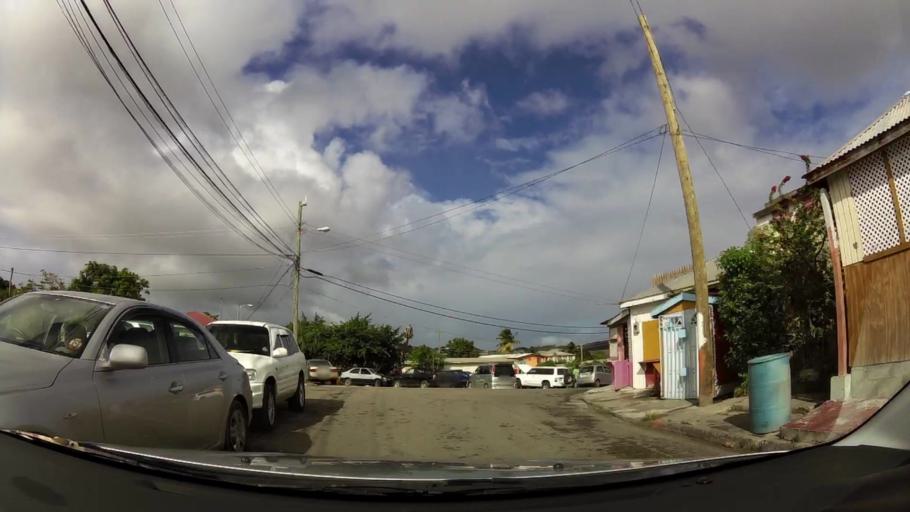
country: AG
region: Saint John
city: Saint John's
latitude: 17.1208
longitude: -61.8247
